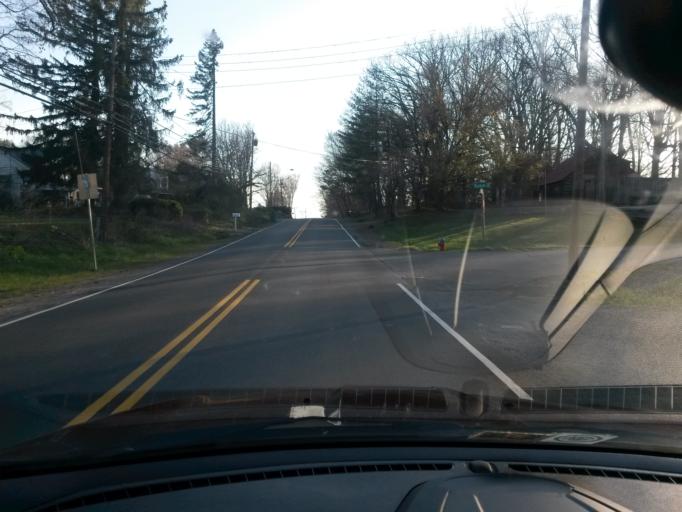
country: US
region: Virginia
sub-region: Montgomery County
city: Christiansburg
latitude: 37.1211
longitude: -80.4188
